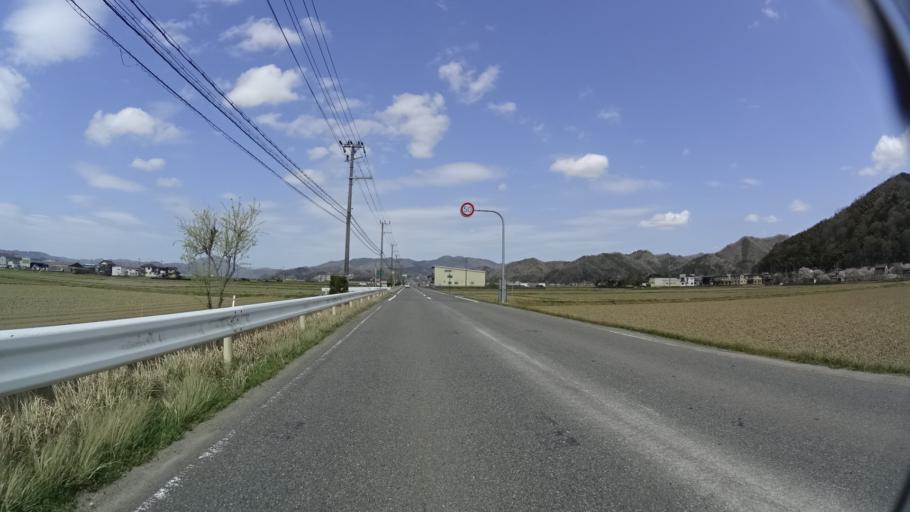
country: JP
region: Hyogo
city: Toyooka
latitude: 35.5219
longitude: 134.8399
